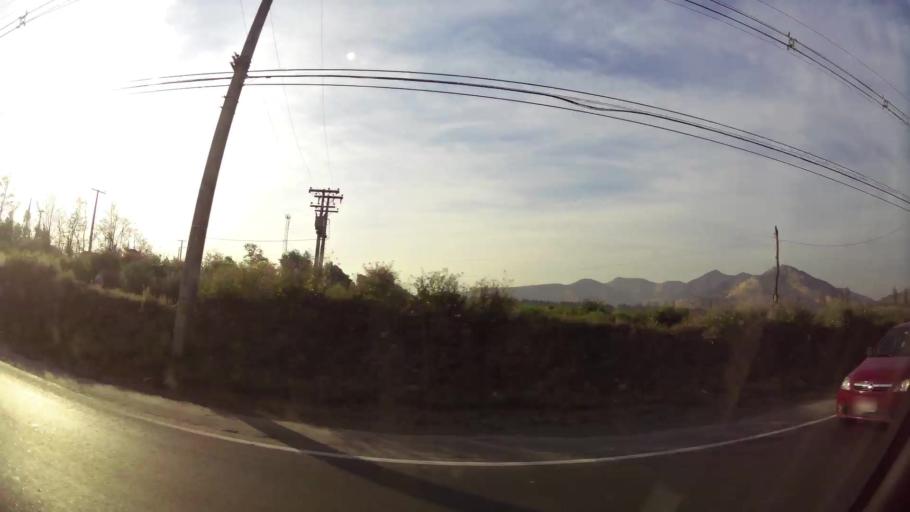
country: CL
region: Santiago Metropolitan
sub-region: Provincia de Maipo
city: San Bernardo
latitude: -33.5564
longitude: -70.7545
